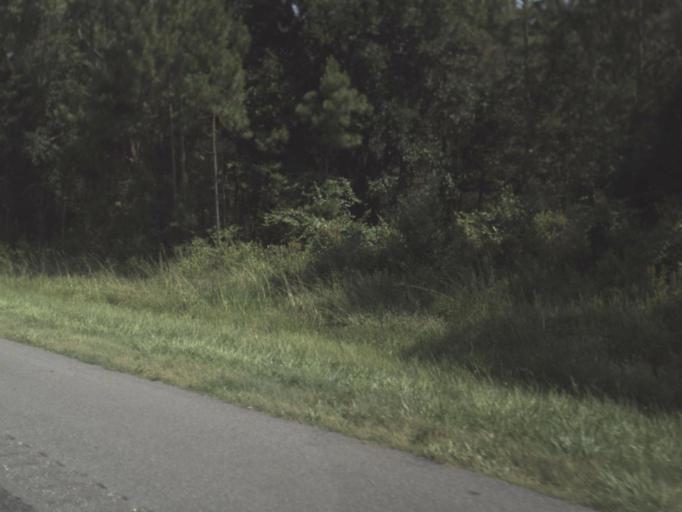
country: US
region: Florida
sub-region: Hamilton County
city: Jasper
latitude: 30.4632
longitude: -82.9566
